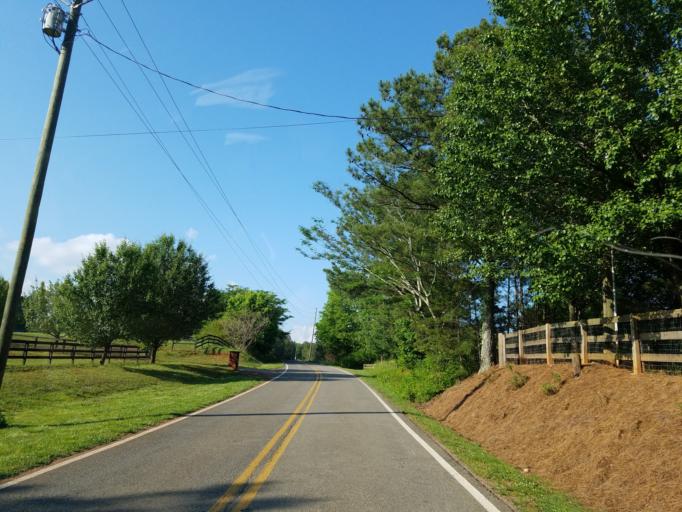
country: US
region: Georgia
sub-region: Pickens County
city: Nelson
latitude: 34.3743
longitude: -84.3251
